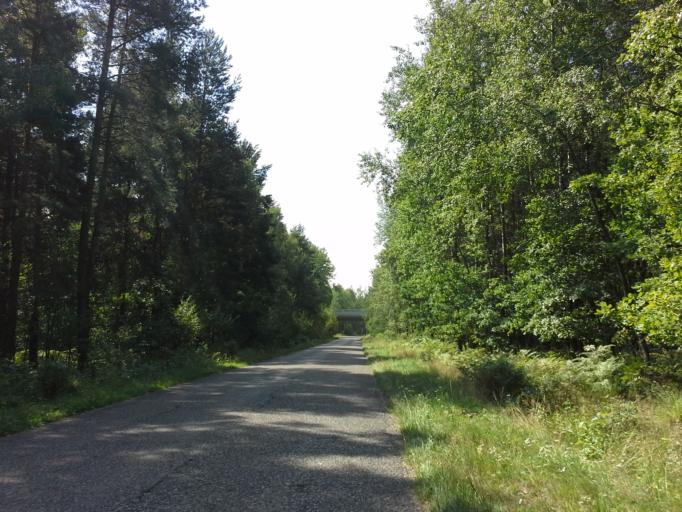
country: PL
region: Lesser Poland Voivodeship
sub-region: Powiat chrzanowski
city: Trzebinia
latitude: 50.1405
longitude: 19.4631
